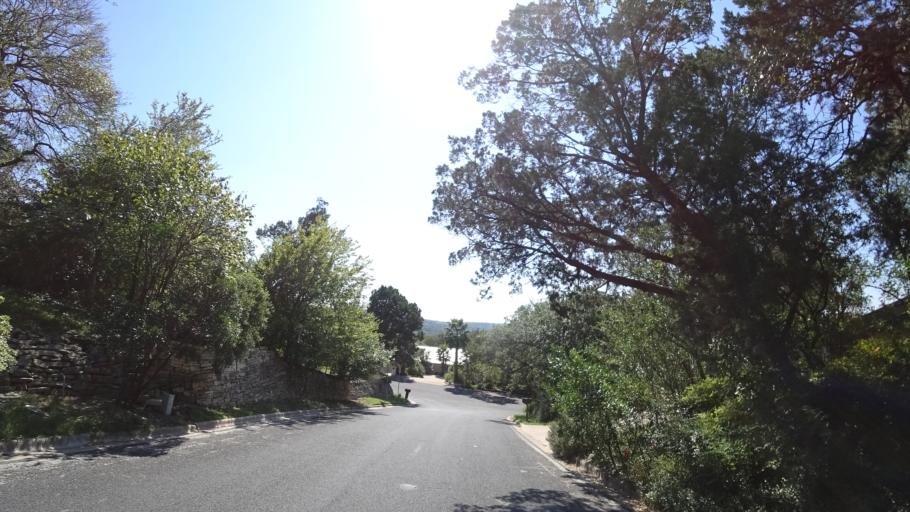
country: US
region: Texas
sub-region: Travis County
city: Rollingwood
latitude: 30.2500
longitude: -97.7918
